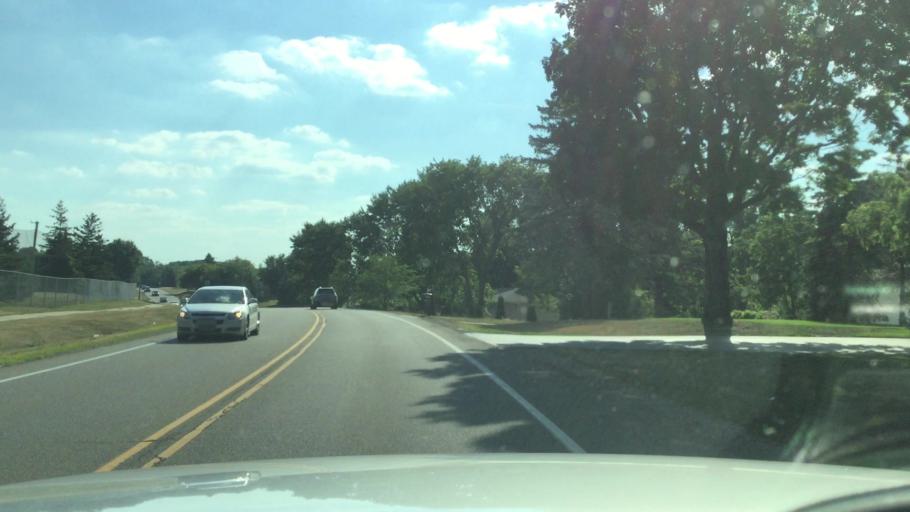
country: US
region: Michigan
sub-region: Genesee County
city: Grand Blanc
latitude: 42.9307
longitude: -83.6005
